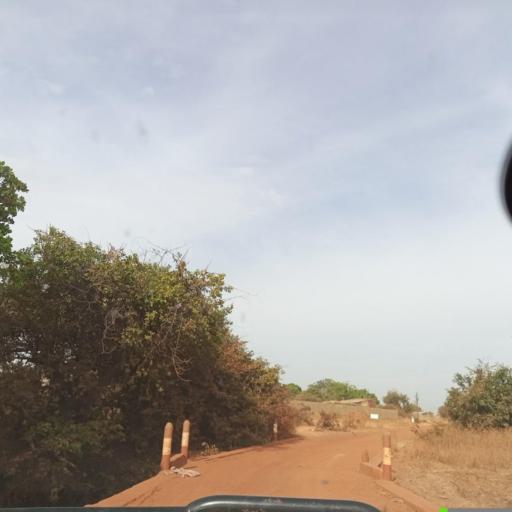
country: ML
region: Koulikoro
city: Koulikoro
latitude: 13.1086
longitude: -7.6489
